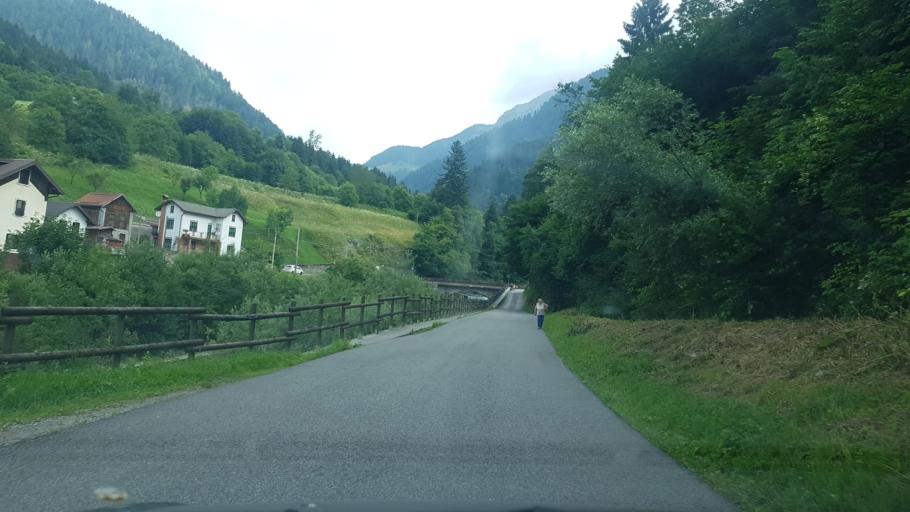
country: IT
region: Friuli Venezia Giulia
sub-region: Provincia di Udine
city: Paularo
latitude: 46.5361
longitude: 13.1189
